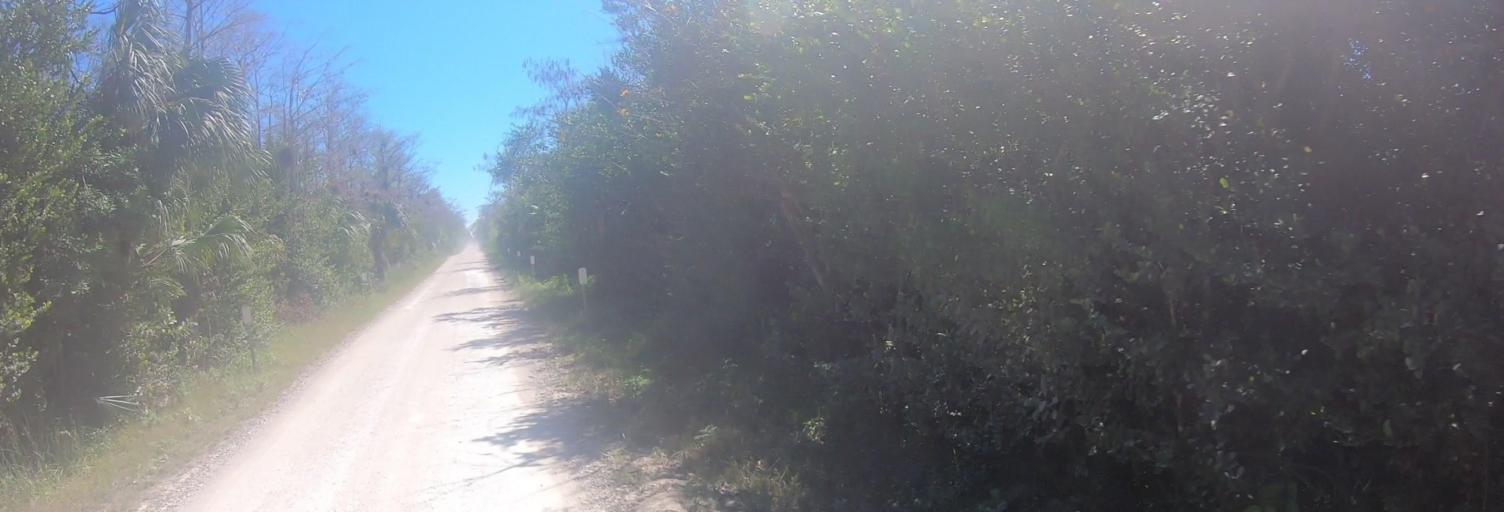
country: US
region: Florida
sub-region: Miami-Dade County
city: The Hammocks
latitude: 25.7566
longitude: -80.9847
